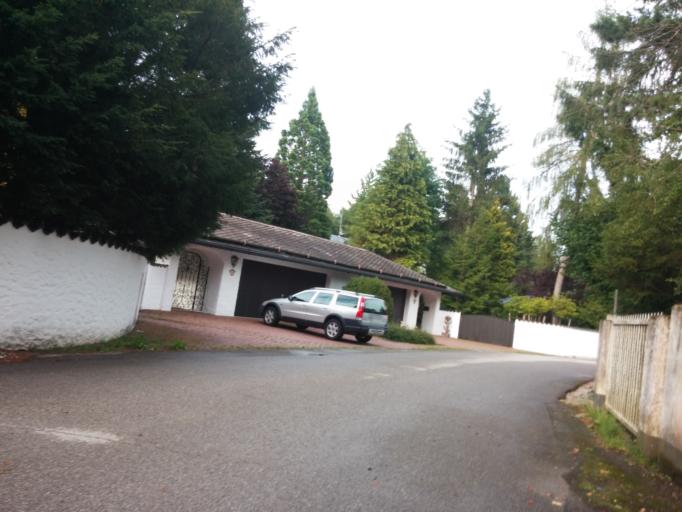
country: DE
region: Bavaria
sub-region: Upper Bavaria
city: Vaterstetten
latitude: 48.0896
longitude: 11.7906
